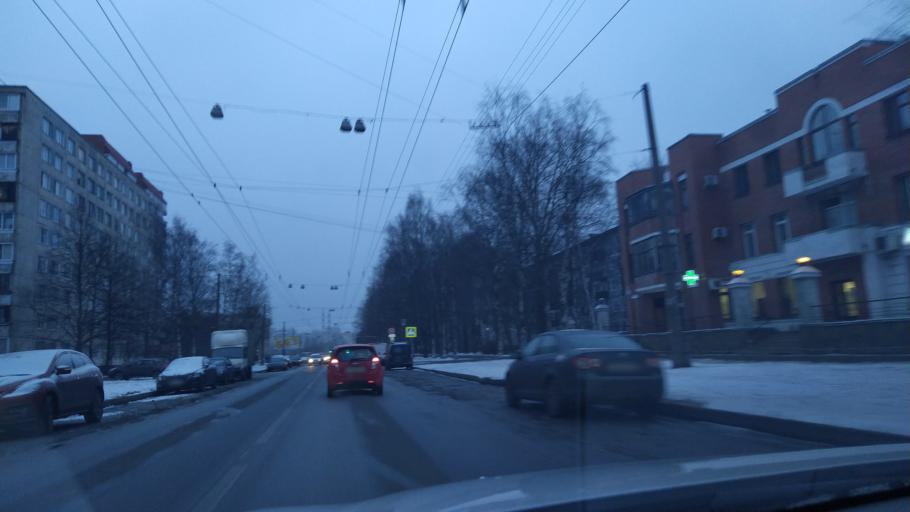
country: RU
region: Leningrad
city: Akademicheskoe
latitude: 60.0164
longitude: 30.4145
